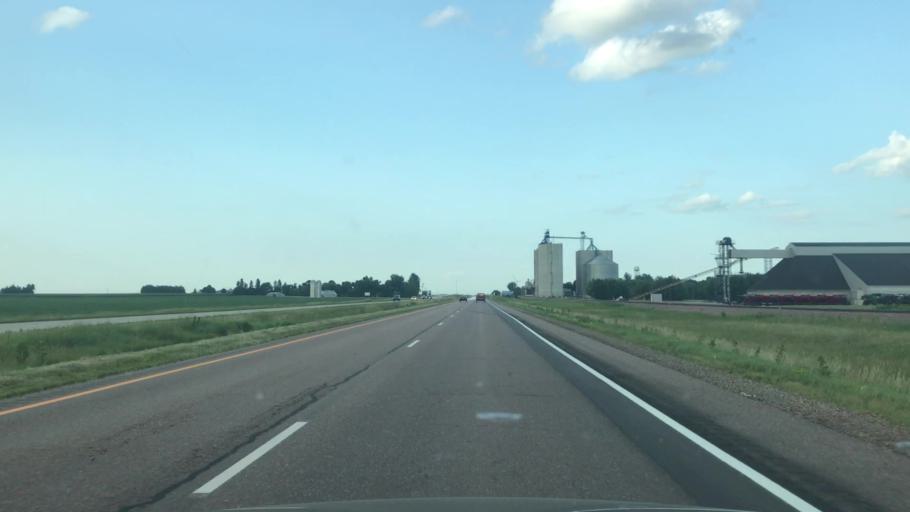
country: US
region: Minnesota
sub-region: Nobles County
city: Worthington
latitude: 43.6931
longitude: -95.4800
